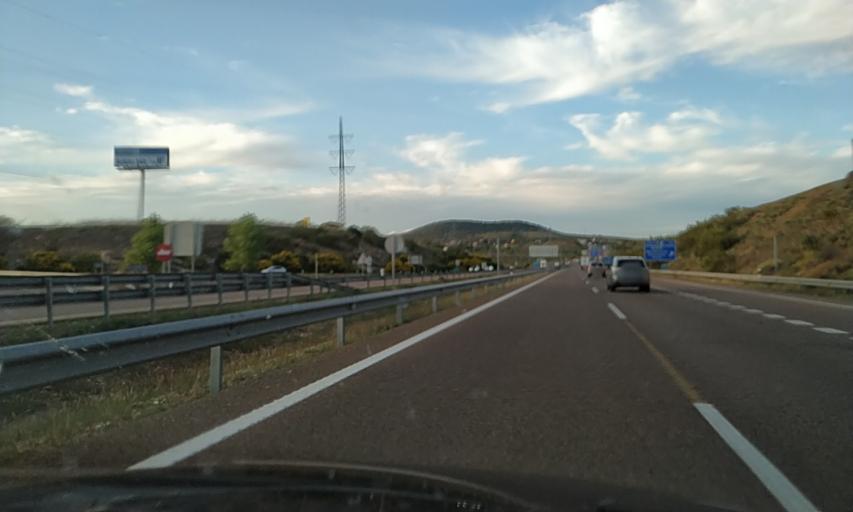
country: ES
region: Extremadura
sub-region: Provincia de Badajoz
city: Merida
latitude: 38.9223
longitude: -6.3714
